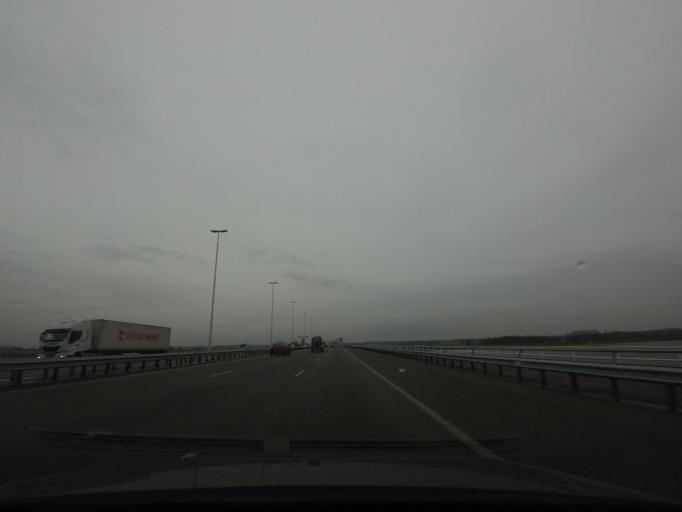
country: NL
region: South Holland
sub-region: Gemeente Strijen
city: Strijen
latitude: 51.7160
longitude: 4.6376
